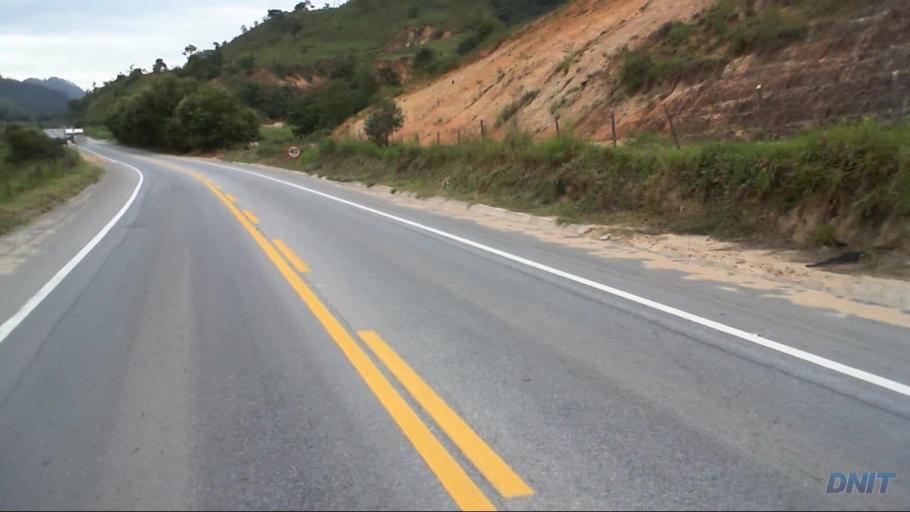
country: BR
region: Minas Gerais
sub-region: Timoteo
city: Timoteo
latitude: -19.6129
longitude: -42.7691
